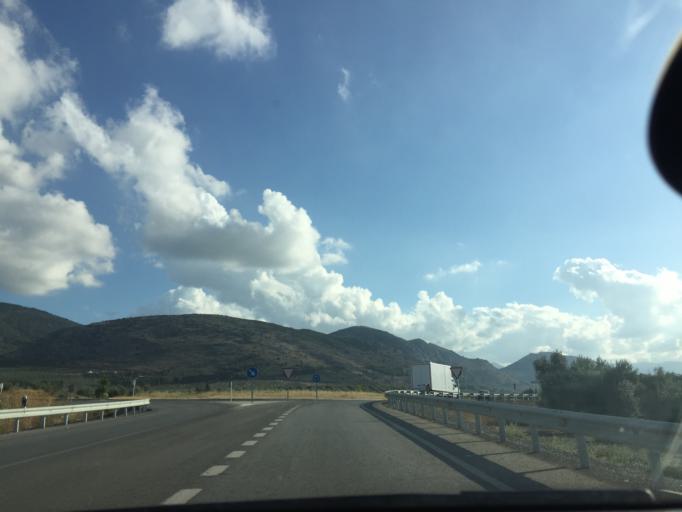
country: ES
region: Andalusia
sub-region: Provincia de Jaen
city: Mancha Real
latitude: 37.7906
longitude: -3.6226
